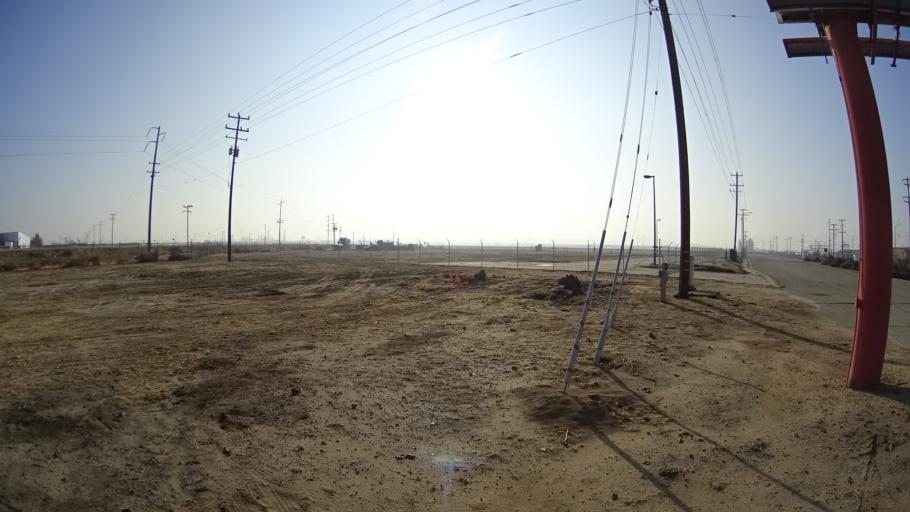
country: US
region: California
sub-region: Kern County
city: Greenacres
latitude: 35.3798
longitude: -119.0921
